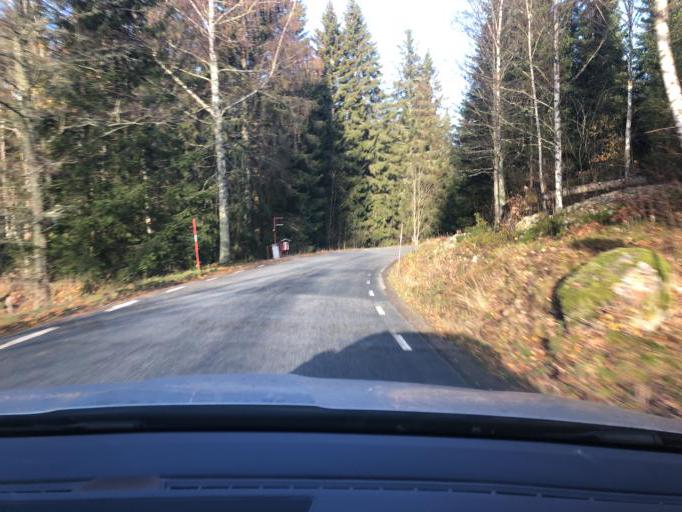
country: SE
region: Soedermanland
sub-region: Flens Kommun
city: Halleforsnas
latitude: 59.1138
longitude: 16.4381
